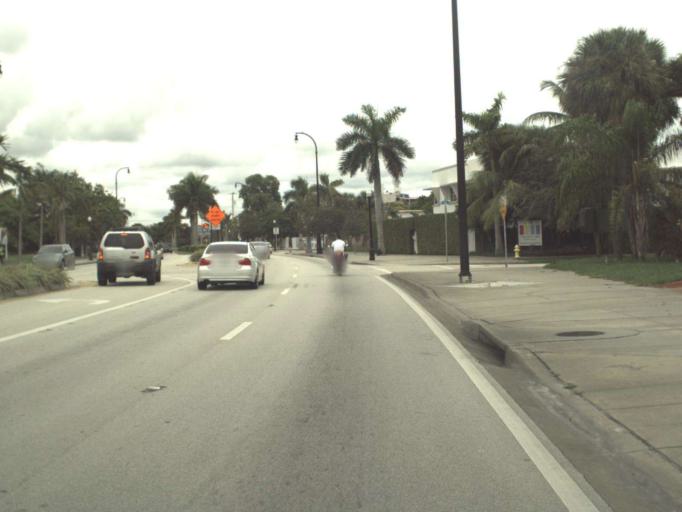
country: US
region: Florida
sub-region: Miami-Dade County
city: El Portal
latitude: 25.8233
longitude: -80.1869
